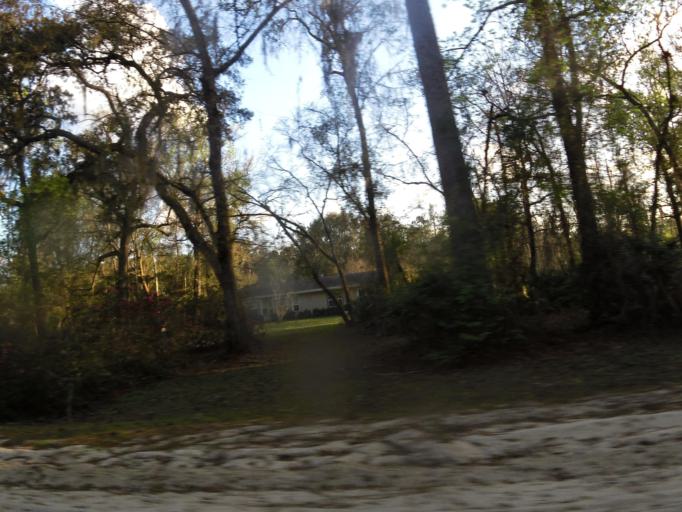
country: US
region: Florida
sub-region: Putnam County
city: Interlachen
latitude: 29.7791
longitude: -81.8550
